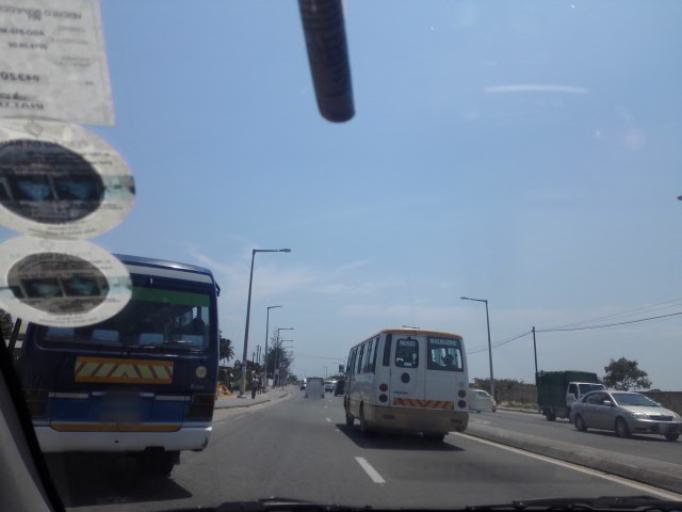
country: MZ
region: Maputo City
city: Maputo
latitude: -25.9218
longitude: 32.5622
